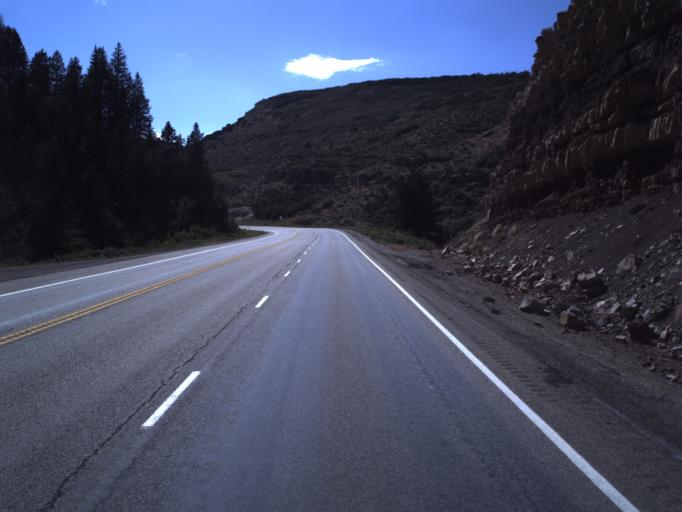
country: US
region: Utah
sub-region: Carbon County
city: Helper
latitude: 40.1945
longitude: -110.9418
